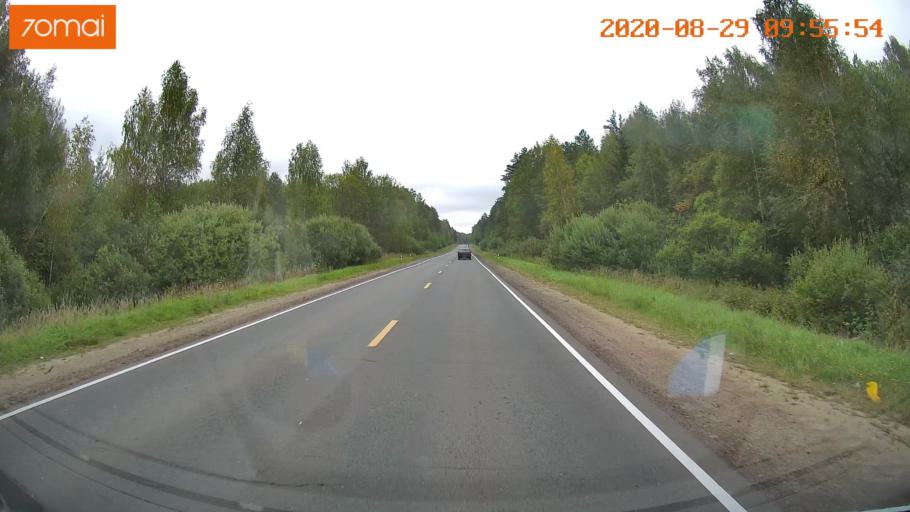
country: RU
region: Ivanovo
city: Zarechnyy
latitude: 57.4216
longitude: 42.2752
